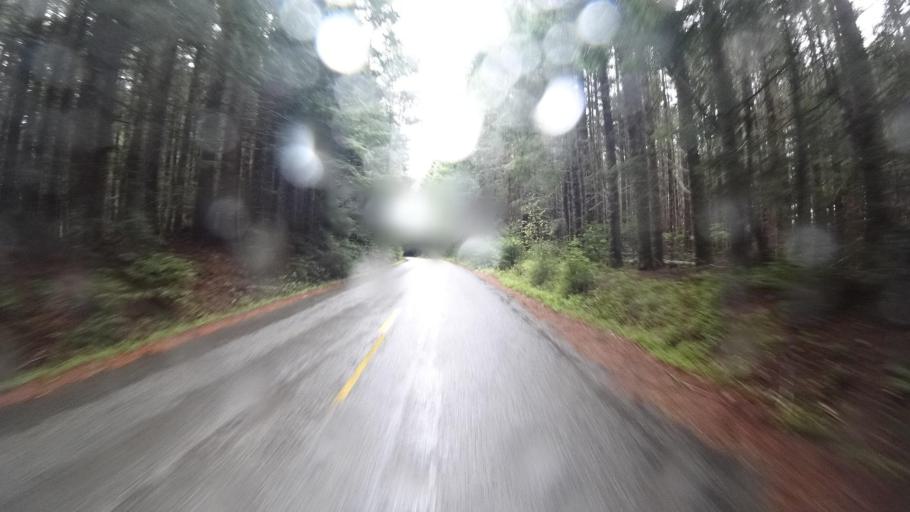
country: US
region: California
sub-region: Humboldt County
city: Westhaven-Moonstone
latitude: 41.2366
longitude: -123.9810
